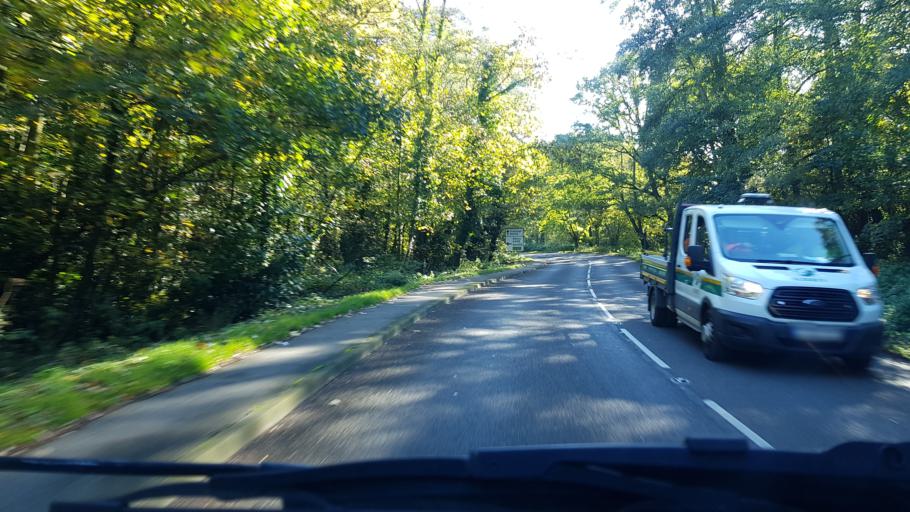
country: GB
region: England
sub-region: Surrey
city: Bramley
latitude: 51.2106
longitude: -0.5514
